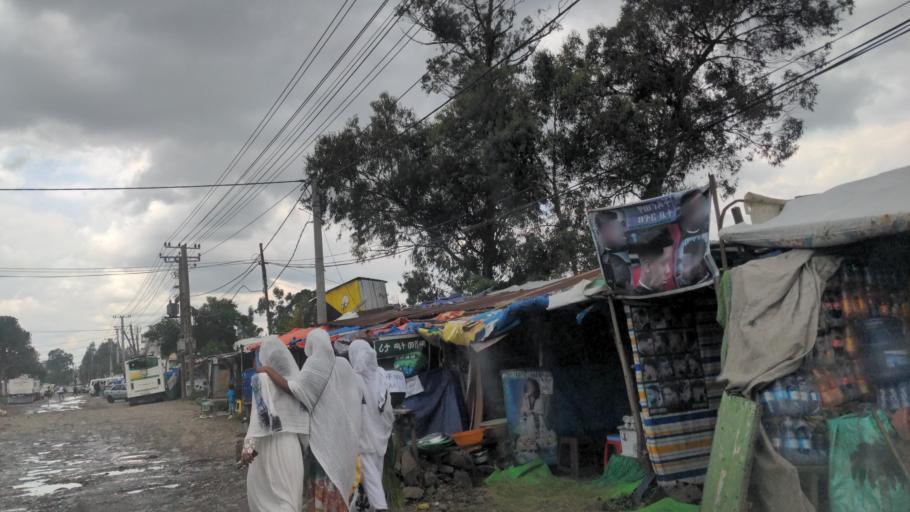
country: ET
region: Adis Abeba
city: Addis Ababa
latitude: 9.0153
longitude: 38.7906
